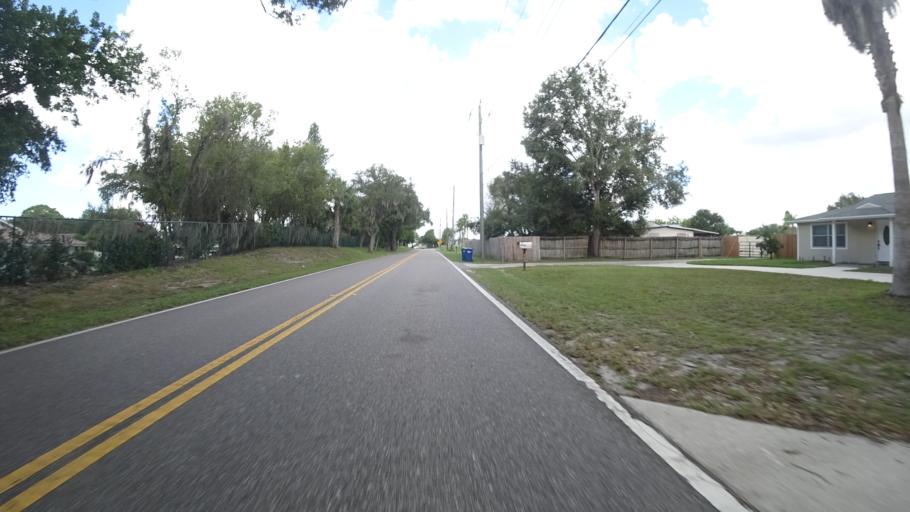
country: US
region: Florida
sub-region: Manatee County
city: Samoset
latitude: 27.4399
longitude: -82.5136
